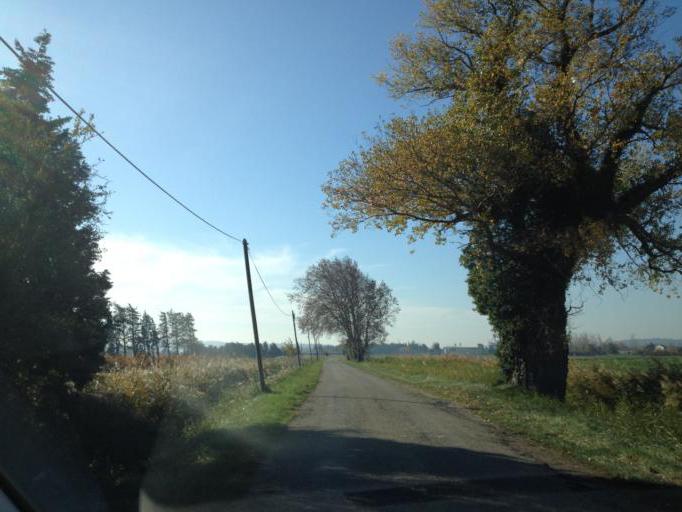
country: FR
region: Provence-Alpes-Cote d'Azur
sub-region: Departement du Vaucluse
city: Bedarrides
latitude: 44.0576
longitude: 4.9182
